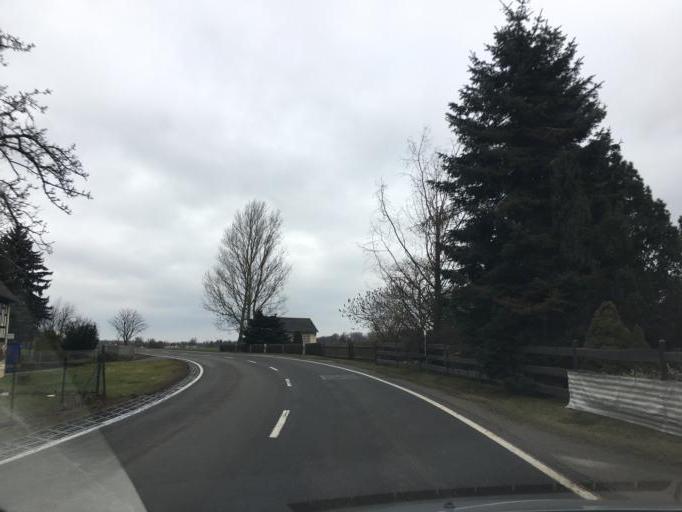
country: DE
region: Thuringia
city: Nobitz
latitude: 50.9519
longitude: 12.5150
